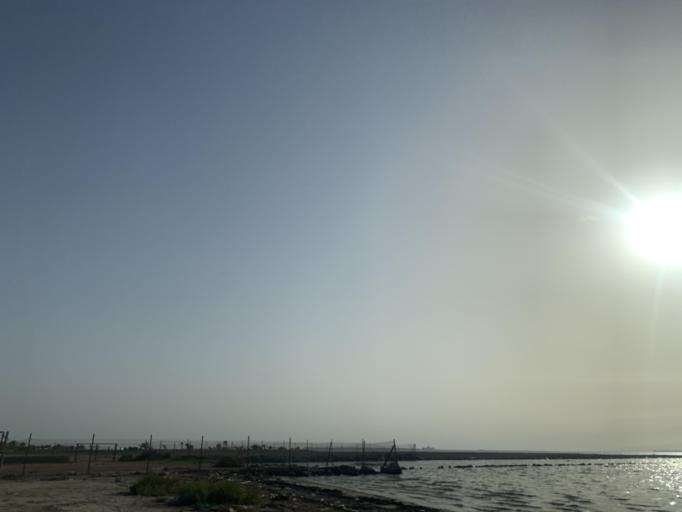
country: BH
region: Central Governorate
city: Madinat Hamad
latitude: 26.1802
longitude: 50.4537
